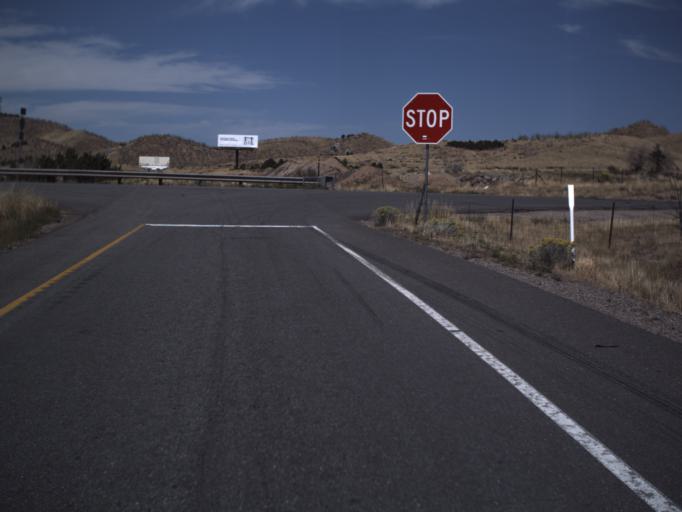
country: US
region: Utah
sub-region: Beaver County
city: Beaver
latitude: 38.6154
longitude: -112.6084
